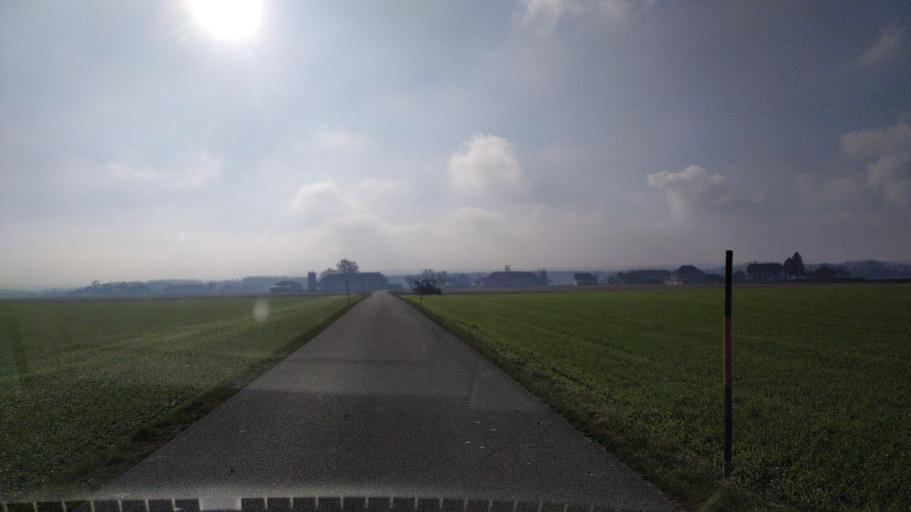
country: AT
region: Upper Austria
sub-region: Politischer Bezirk Perg
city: Perg
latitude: 48.1925
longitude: 14.6546
